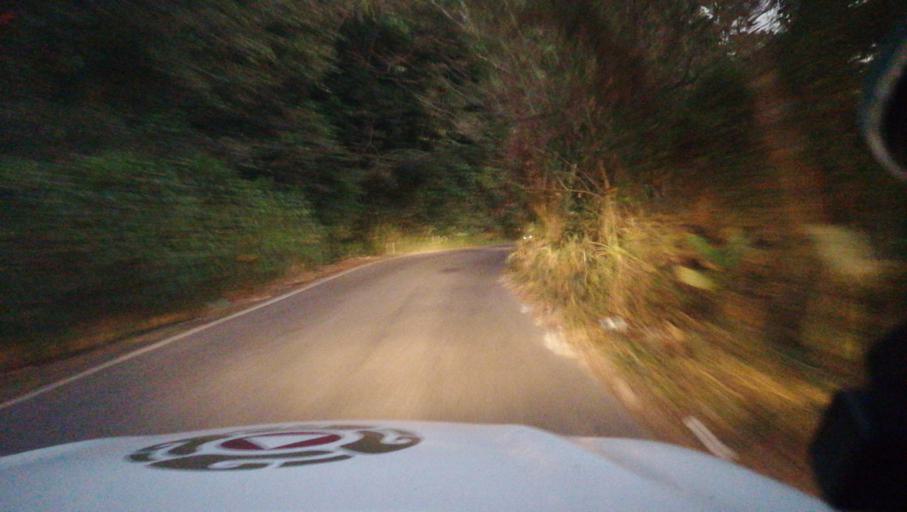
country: MX
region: Chiapas
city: Veinte de Noviembre
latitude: 14.9704
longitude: -92.2519
